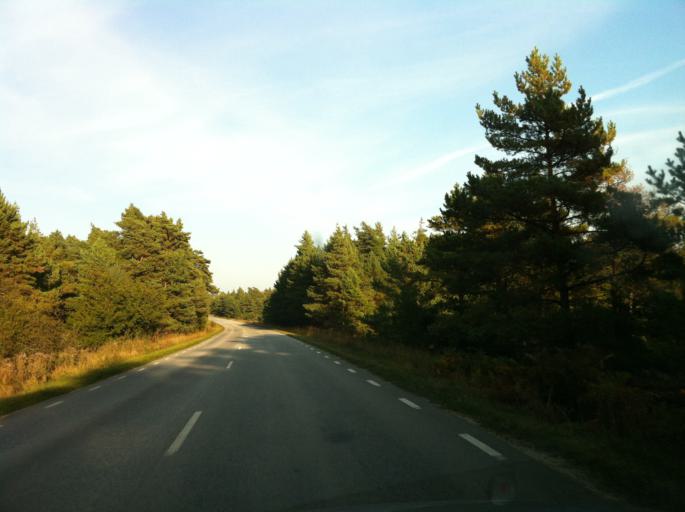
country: SE
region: Gotland
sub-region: Gotland
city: Slite
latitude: 57.4261
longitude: 18.7865
